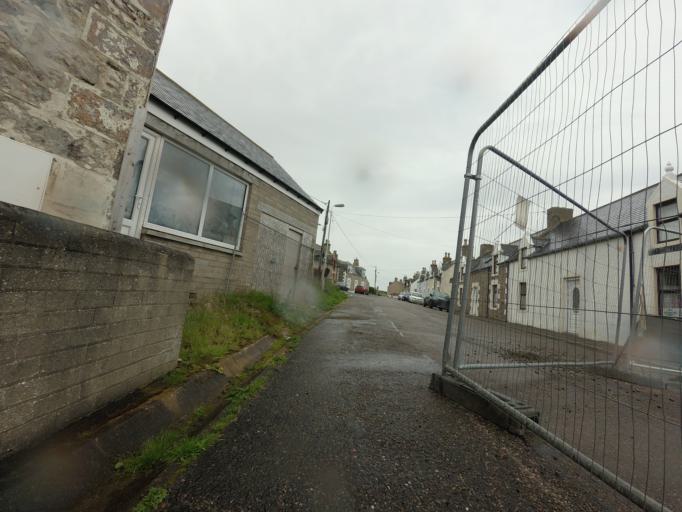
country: GB
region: Scotland
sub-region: Moray
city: Portknockie
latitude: 57.7031
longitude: -2.8624
